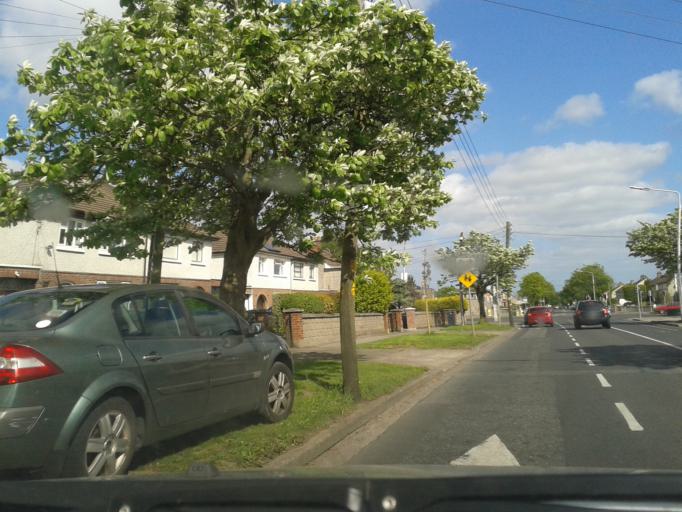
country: IE
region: Leinster
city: Ballymun
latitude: 53.3895
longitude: -6.2661
